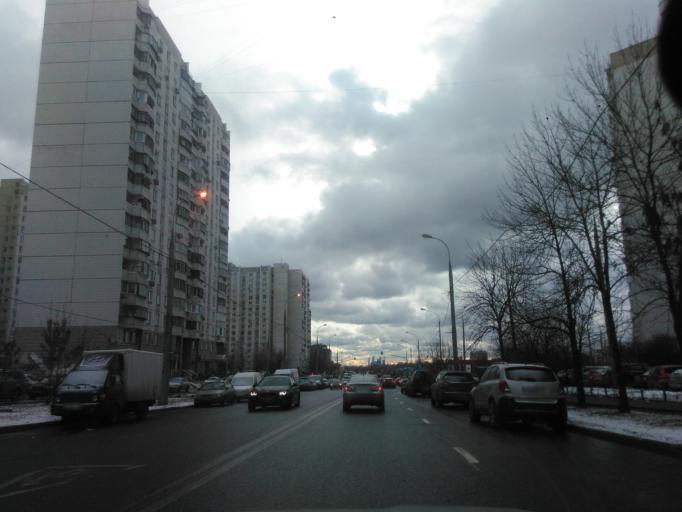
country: RU
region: Moskovskaya
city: Pavshino
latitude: 55.8437
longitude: 37.3513
